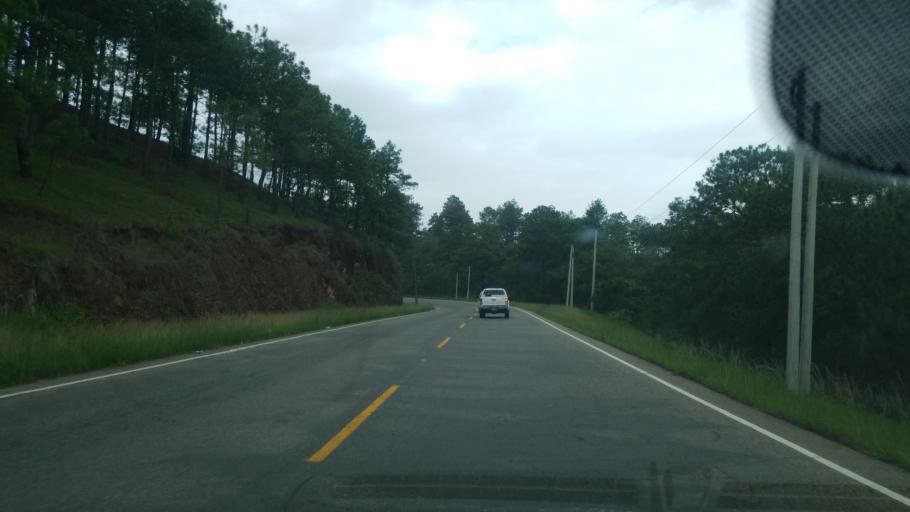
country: HN
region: Ocotepeque
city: Sinuapa
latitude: 14.4614
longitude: -89.1630
